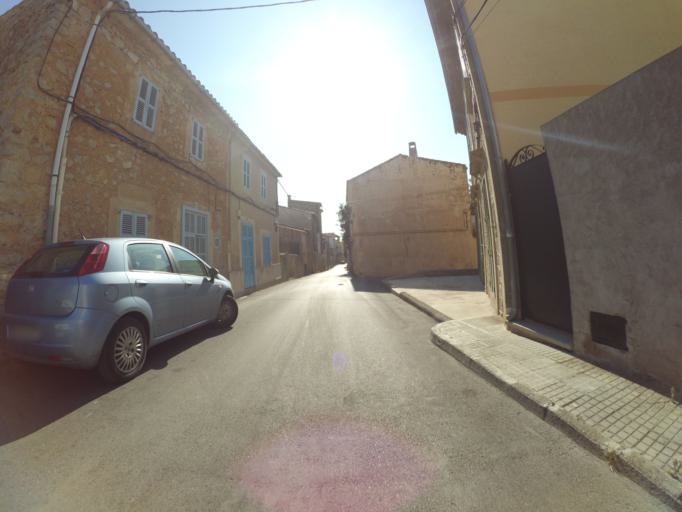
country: ES
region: Balearic Islands
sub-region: Illes Balears
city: Arta
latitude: 39.6960
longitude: 3.3478
